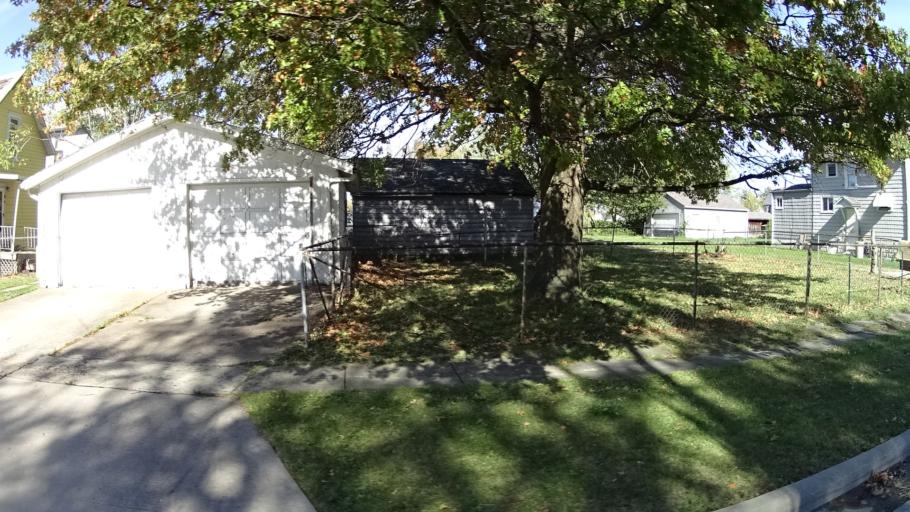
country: US
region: Ohio
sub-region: Lorain County
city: Lorain
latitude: 41.4526
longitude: -82.1817
